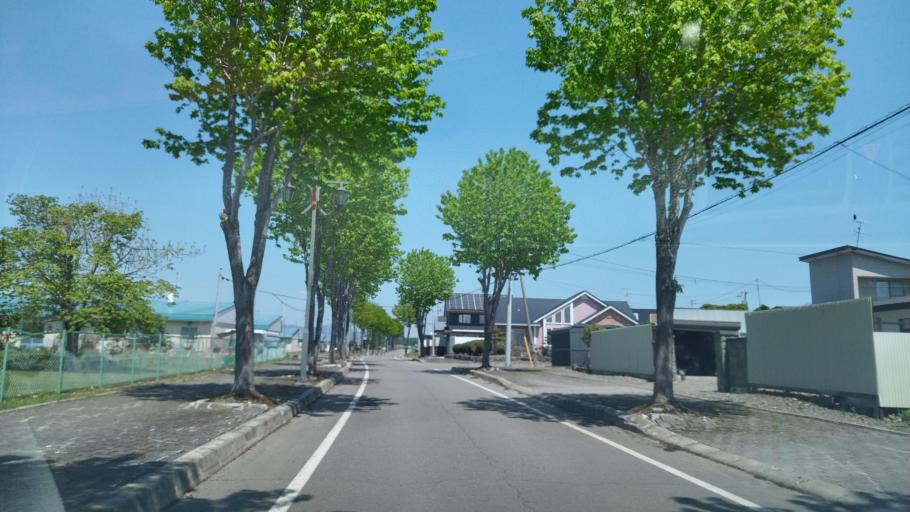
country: JP
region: Hokkaido
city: Otofuke
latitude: 43.1713
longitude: 143.2511
